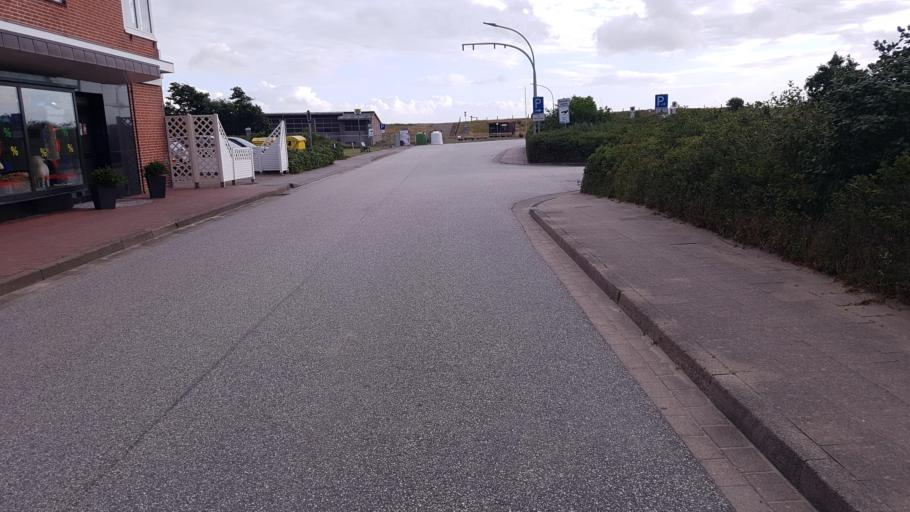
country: DE
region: Schleswig-Holstein
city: Sankt Peter-Ording
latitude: 54.2827
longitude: 8.6653
